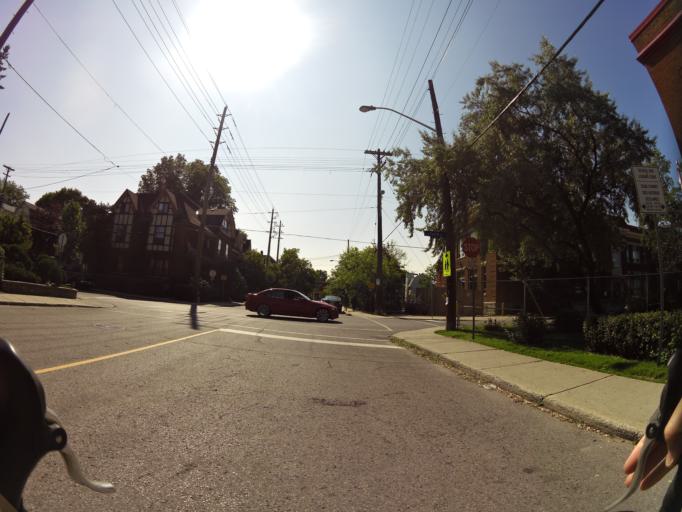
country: CA
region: Ontario
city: Ottawa
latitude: 45.4015
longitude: -75.6906
